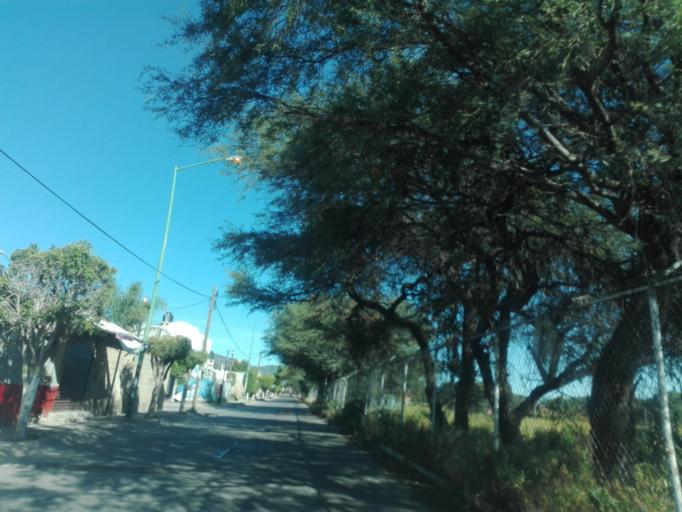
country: MX
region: Guanajuato
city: Leon
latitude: 21.1925
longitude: -101.6776
